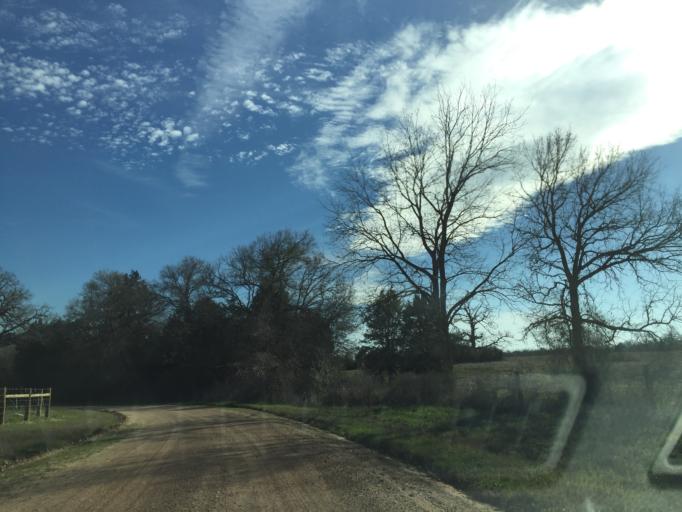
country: US
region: Texas
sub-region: Milam County
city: Thorndale
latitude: 30.4481
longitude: -97.1783
